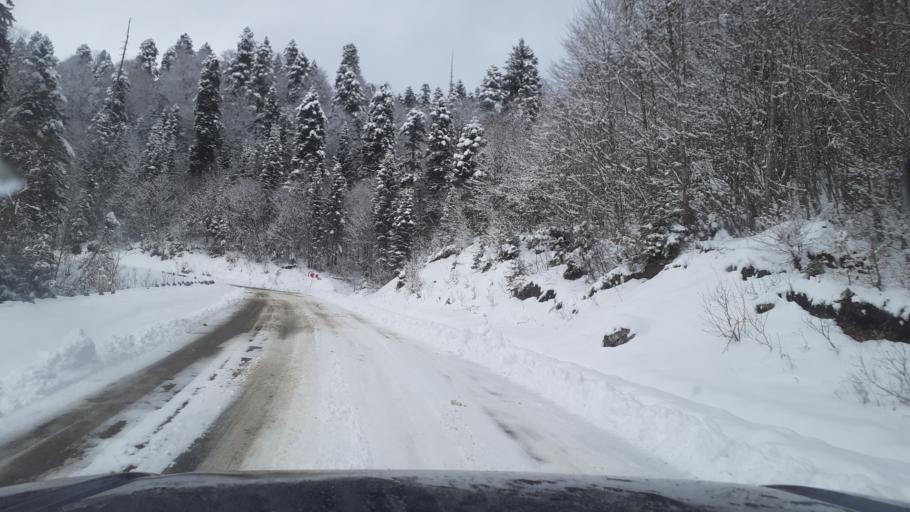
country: RU
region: Adygeya
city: Kamennomostskiy
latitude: 44.0086
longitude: 40.0151
